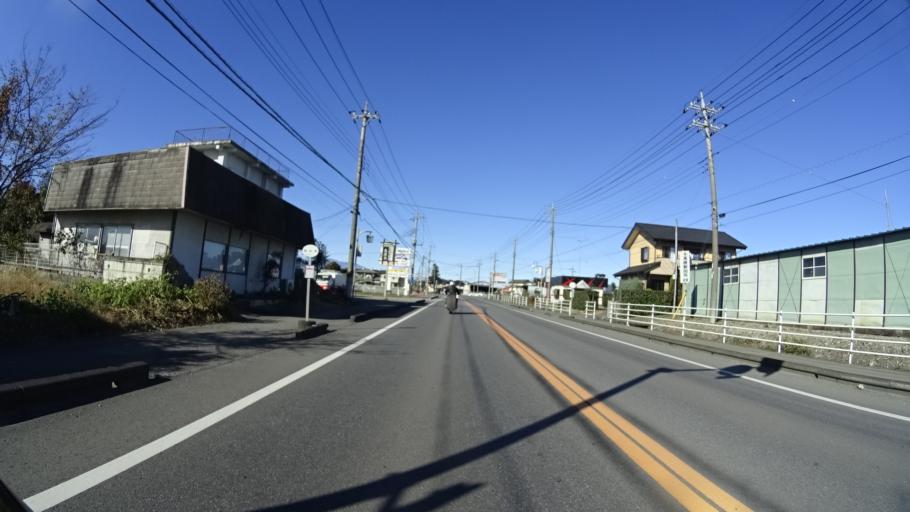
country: JP
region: Tochigi
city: Kanuma
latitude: 36.5279
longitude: 139.7489
